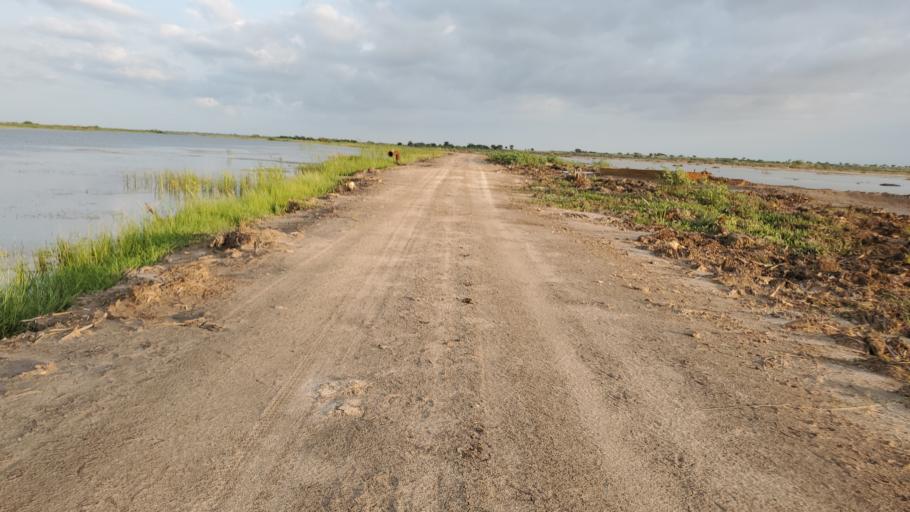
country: SN
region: Saint-Louis
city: Saint-Louis
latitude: 16.0218
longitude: -16.4082
